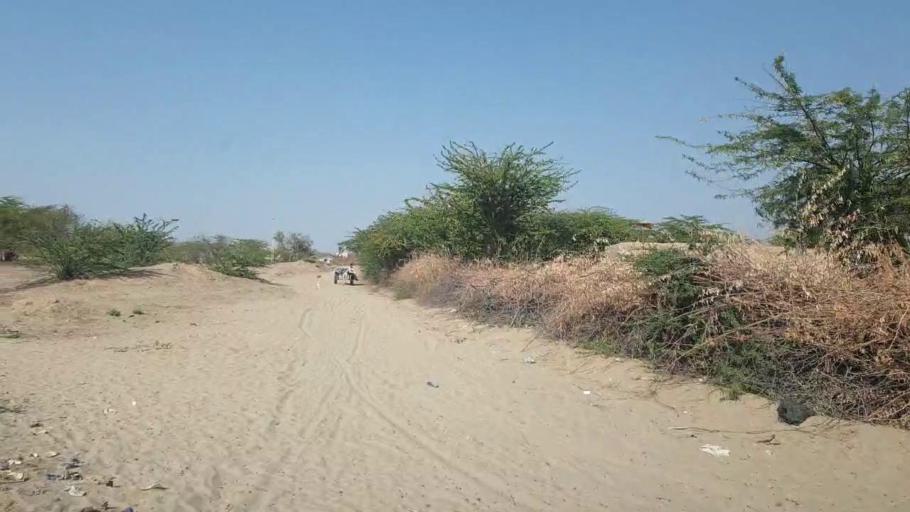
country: PK
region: Sindh
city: Dhoro Naro
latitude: 25.5039
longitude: 69.6027
